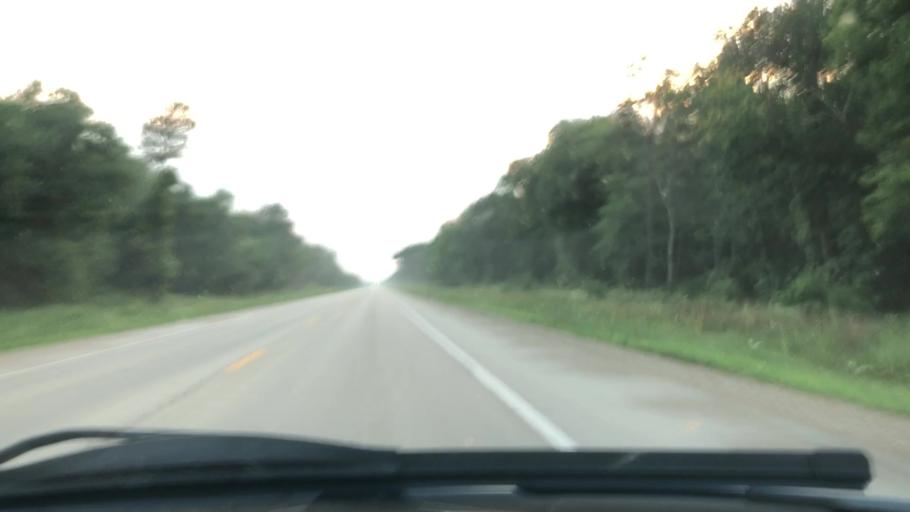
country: US
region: Wisconsin
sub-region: Sauk County
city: Spring Green
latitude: 43.1911
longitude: -90.1754
